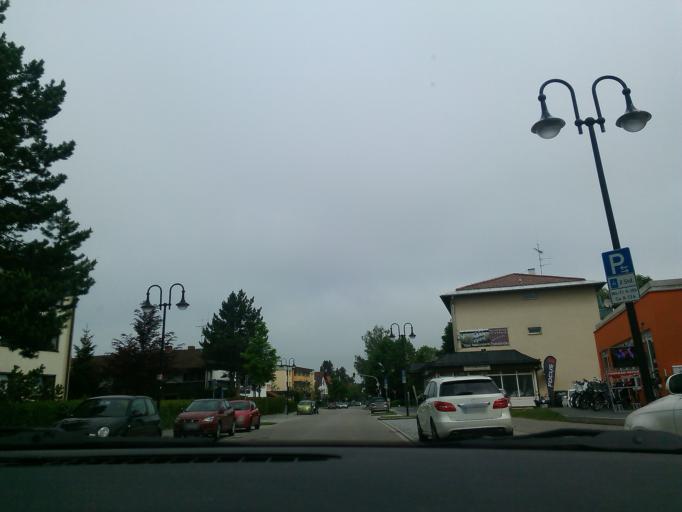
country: DE
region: Bavaria
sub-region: Upper Bavaria
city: Eichenau
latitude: 48.1663
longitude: 11.3243
